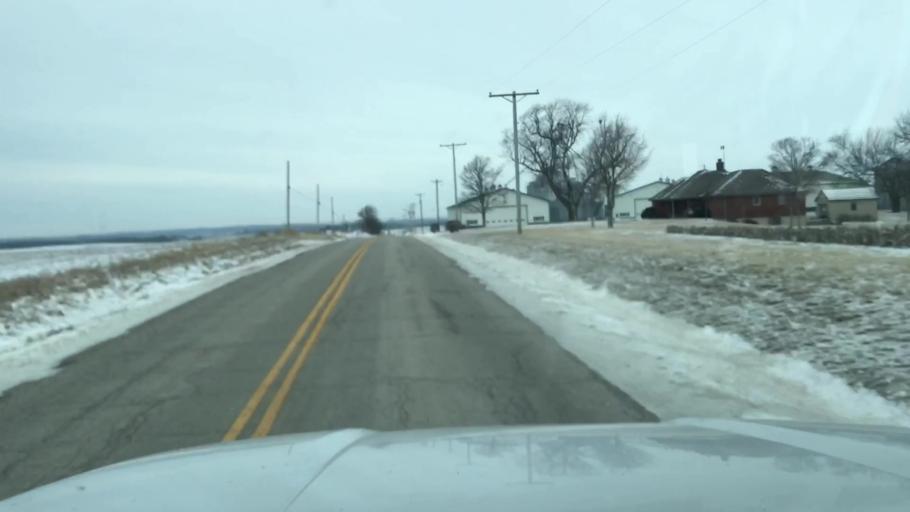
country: US
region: Missouri
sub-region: Andrew County
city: Savannah
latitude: 40.0248
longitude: -94.9366
